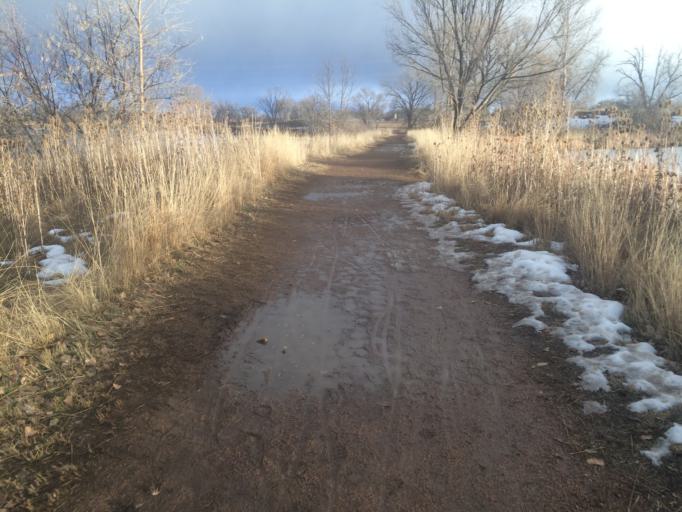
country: US
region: Colorado
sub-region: Boulder County
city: Gunbarrel
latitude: 40.0399
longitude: -105.1883
